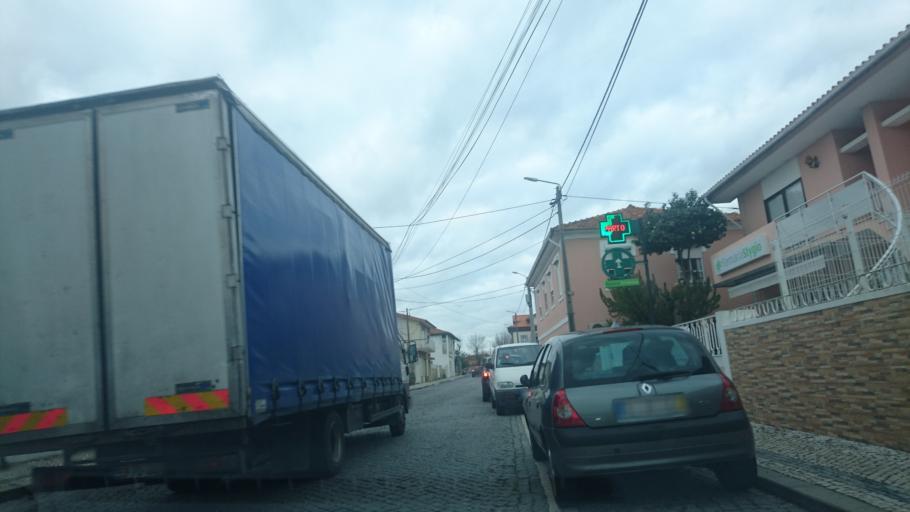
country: PT
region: Aveiro
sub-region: Santa Maria da Feira
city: Pacos de Brandao
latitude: 40.9727
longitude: -8.5898
